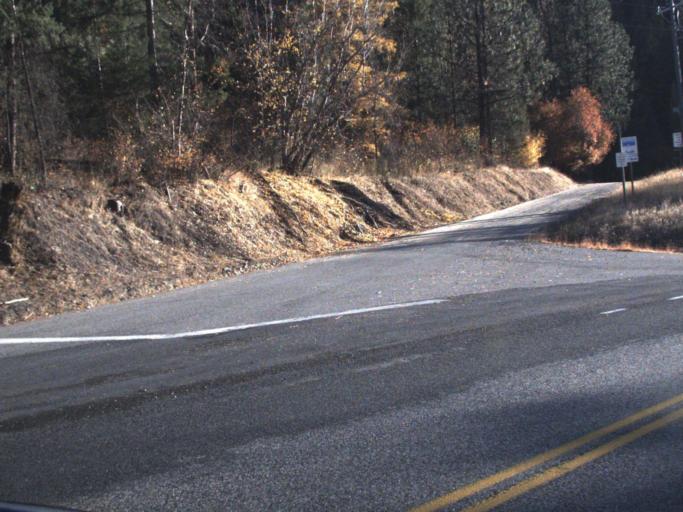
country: CA
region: British Columbia
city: Rossland
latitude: 48.8717
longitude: -117.8415
